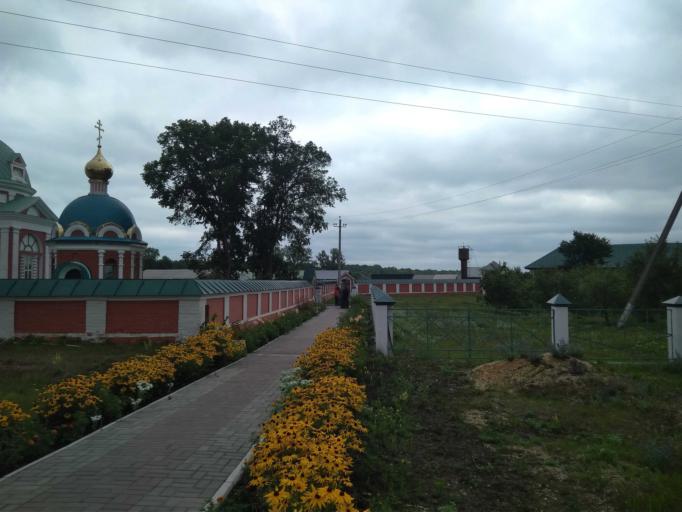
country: RU
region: Mordoviya
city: Temnikov
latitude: 54.6531
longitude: 43.1631
